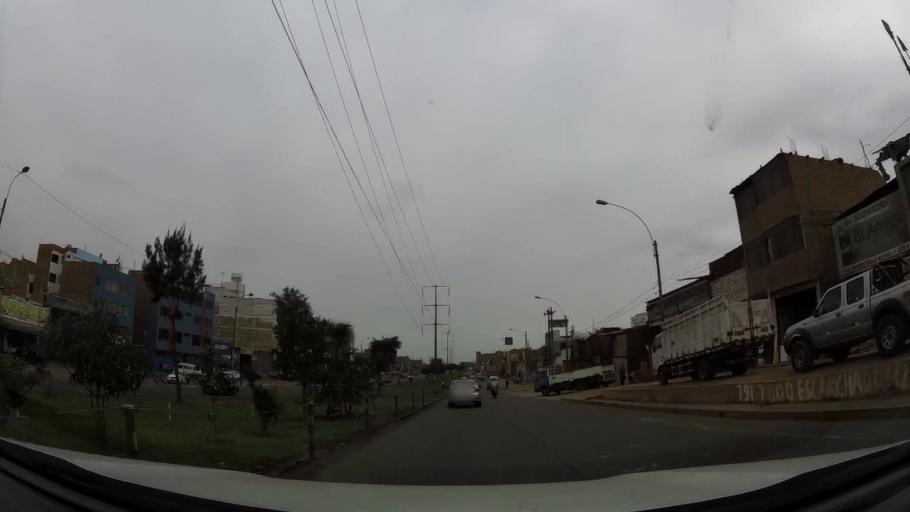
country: PE
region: Lima
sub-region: Lima
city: Independencia
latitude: -11.9849
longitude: -77.0790
